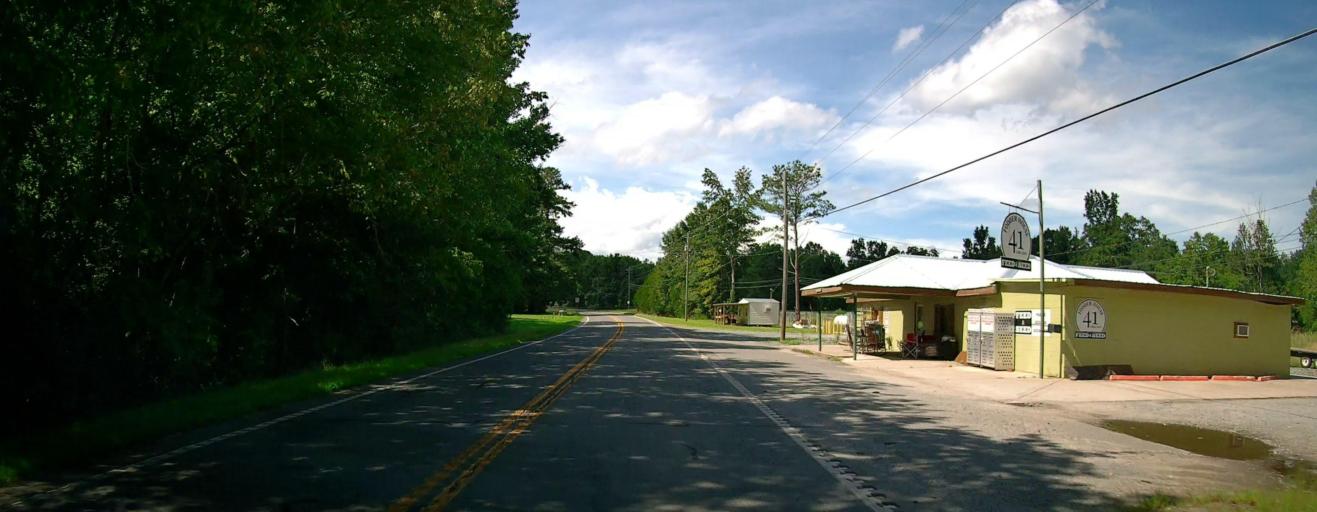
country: US
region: Georgia
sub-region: Talbot County
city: Sardis
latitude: 32.7913
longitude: -84.5643
